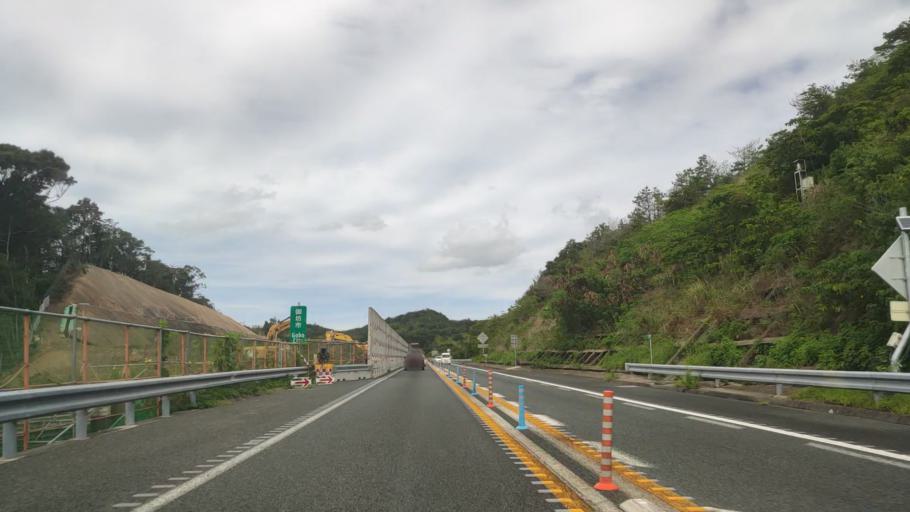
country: JP
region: Wakayama
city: Gobo
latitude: 33.8714
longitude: 135.1888
